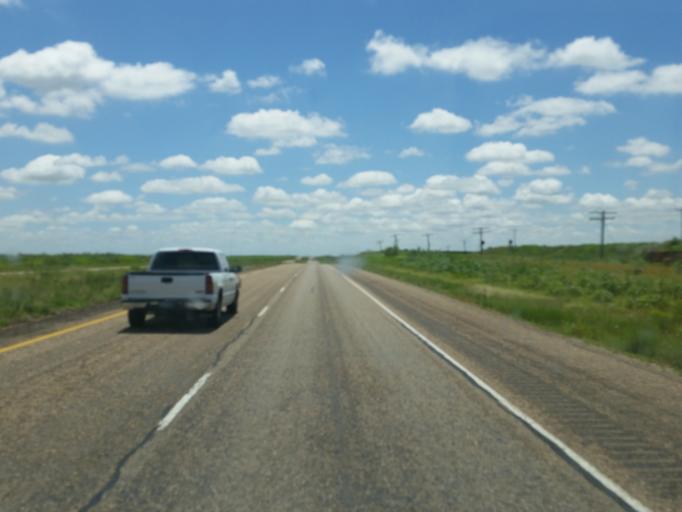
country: US
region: Texas
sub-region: Garza County
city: Post
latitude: 33.1274
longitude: -101.2943
